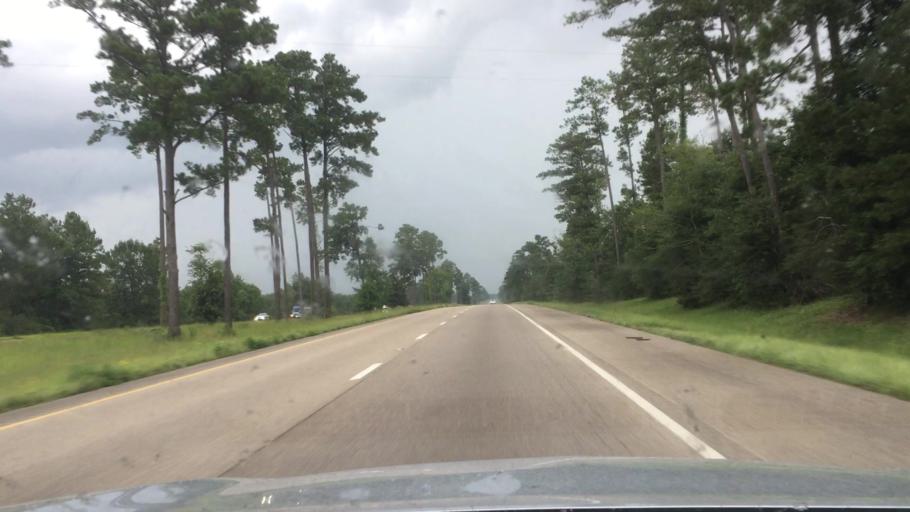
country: US
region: Mississippi
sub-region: Pearl River County
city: Carriere
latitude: 30.7028
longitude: -89.5612
